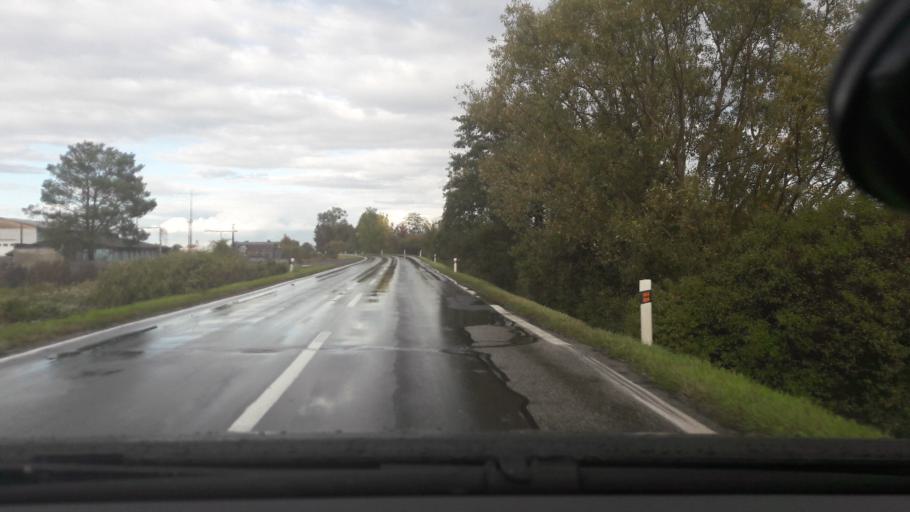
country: CZ
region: South Moravian
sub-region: Okres Breclav
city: Lanzhot
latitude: 48.6437
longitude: 17.0071
